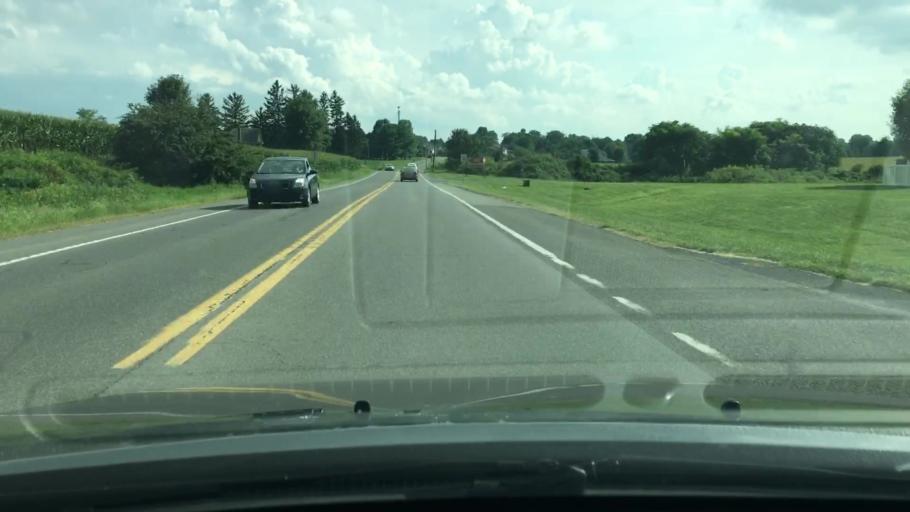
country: US
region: Pennsylvania
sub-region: Franklin County
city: Guilford
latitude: 39.9330
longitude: -77.5905
